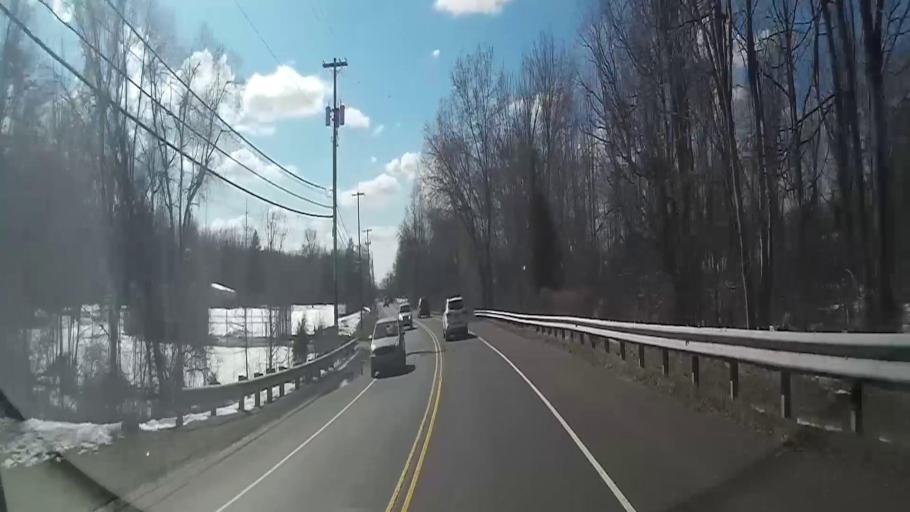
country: US
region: New Jersey
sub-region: Burlington County
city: Marlton
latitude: 39.8862
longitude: -74.8929
